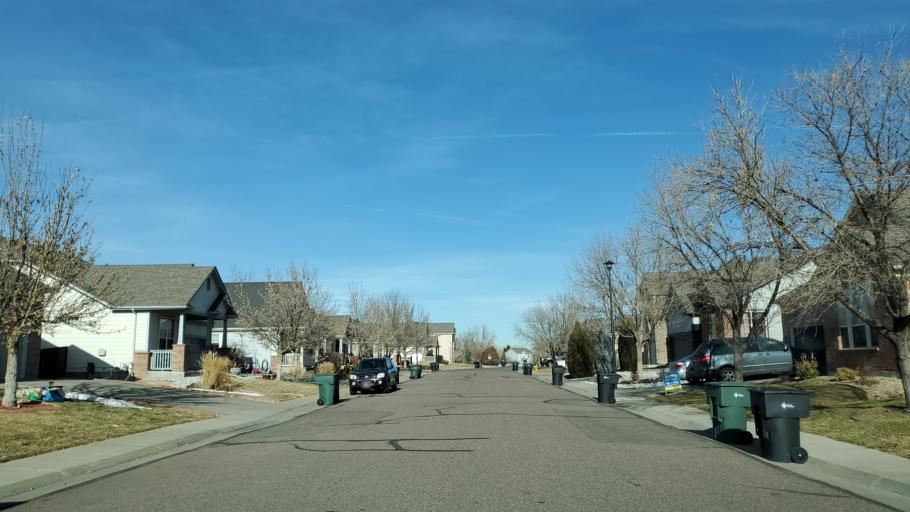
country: US
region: Colorado
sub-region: Adams County
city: Northglenn
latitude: 39.9182
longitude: -104.9491
